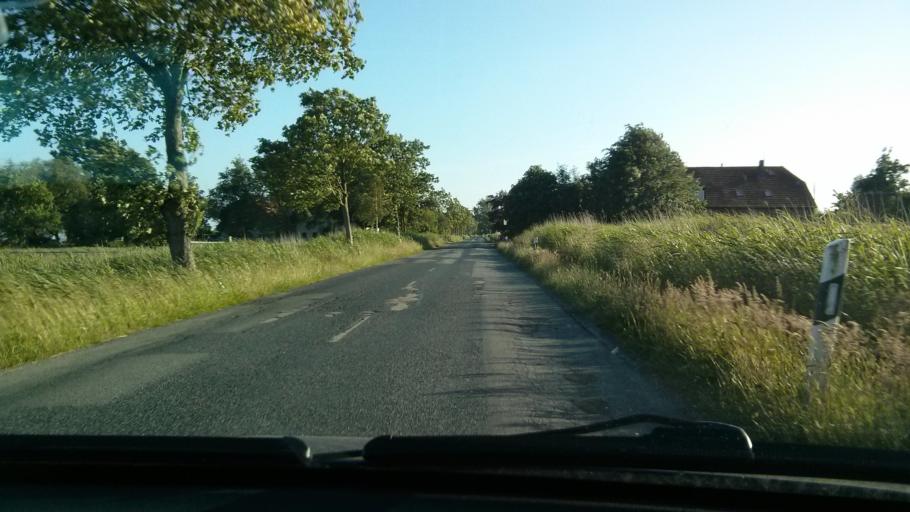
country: DE
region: Lower Saxony
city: Nordenham
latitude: 53.4749
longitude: 8.5478
